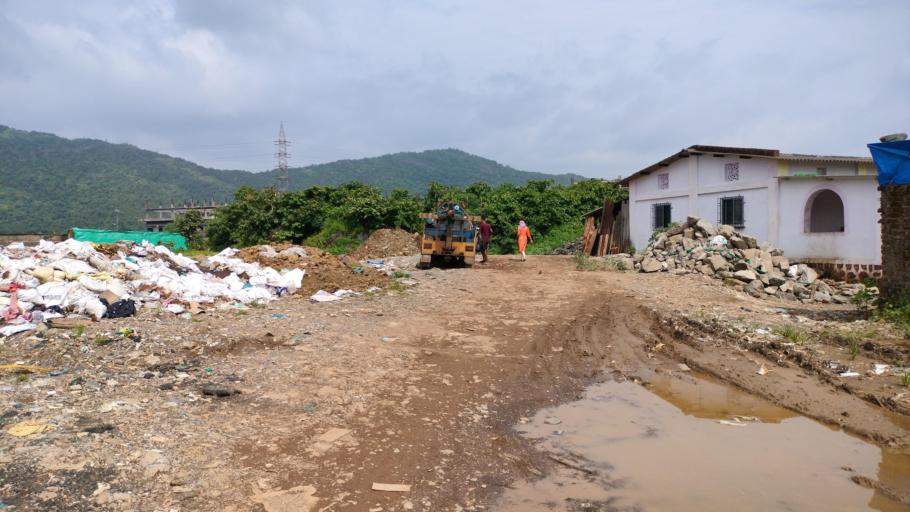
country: IN
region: Maharashtra
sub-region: Thane
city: Bhayandar
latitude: 19.3872
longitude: 72.8988
